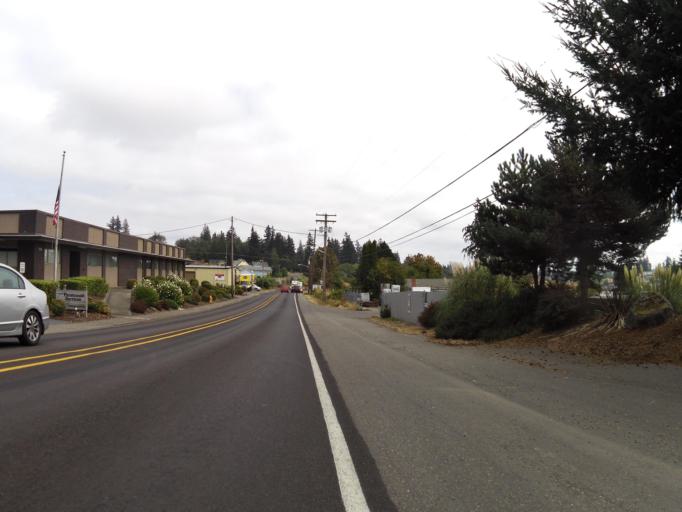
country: US
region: Washington
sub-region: Kitsap County
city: Navy Yard City
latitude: 47.5626
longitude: -122.6781
